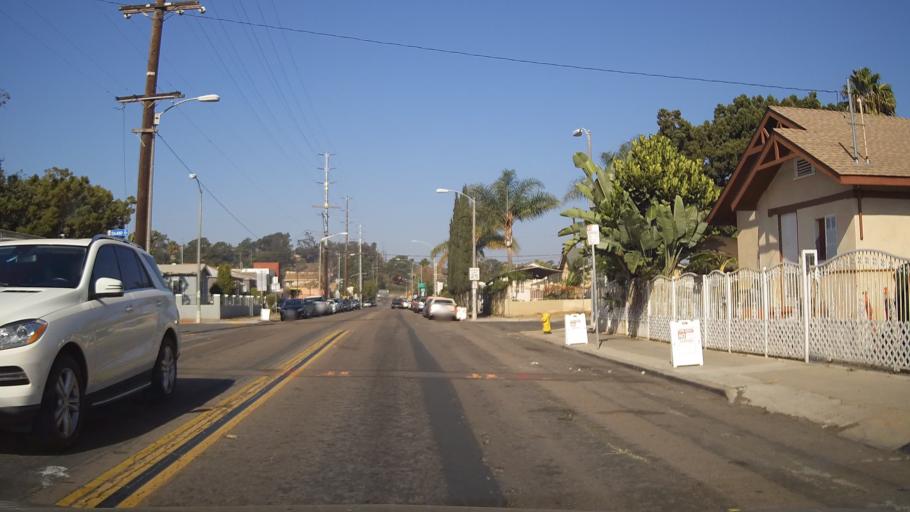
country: US
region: California
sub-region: San Diego County
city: San Diego
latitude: 32.7104
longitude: -117.1251
